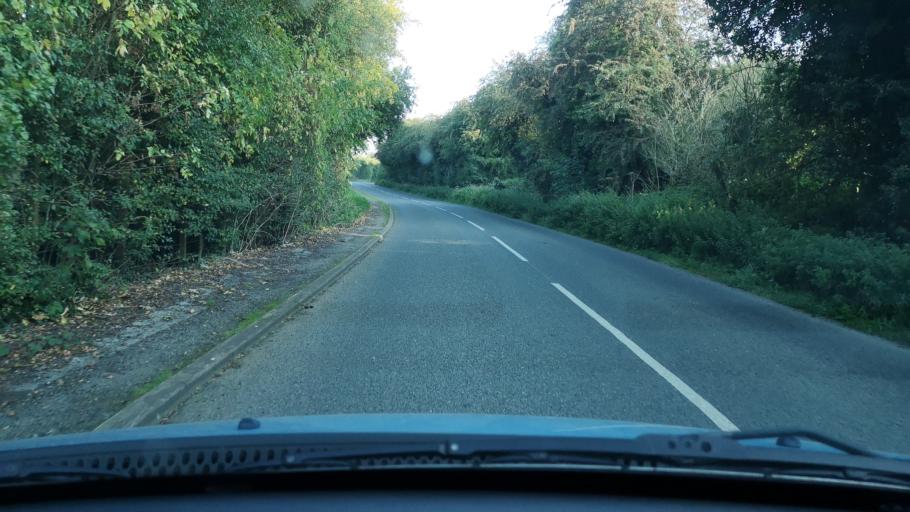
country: GB
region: England
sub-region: Doncaster
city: Norton
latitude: 53.6721
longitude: -1.2081
